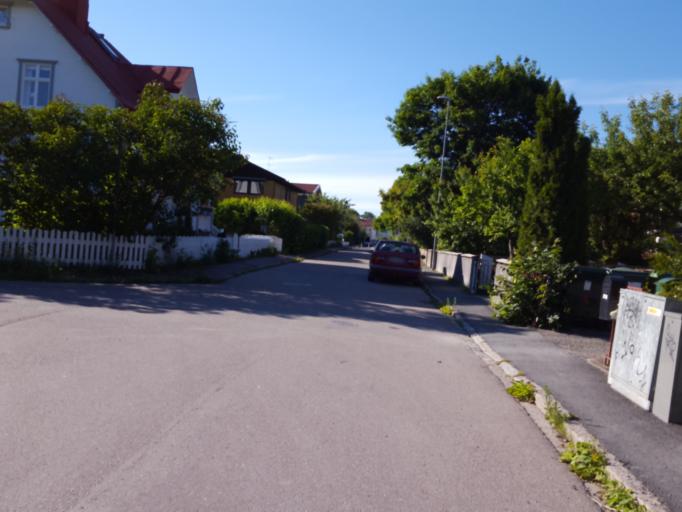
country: SE
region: Uppsala
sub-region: Uppsala Kommun
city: Uppsala
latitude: 59.8615
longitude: 17.6623
